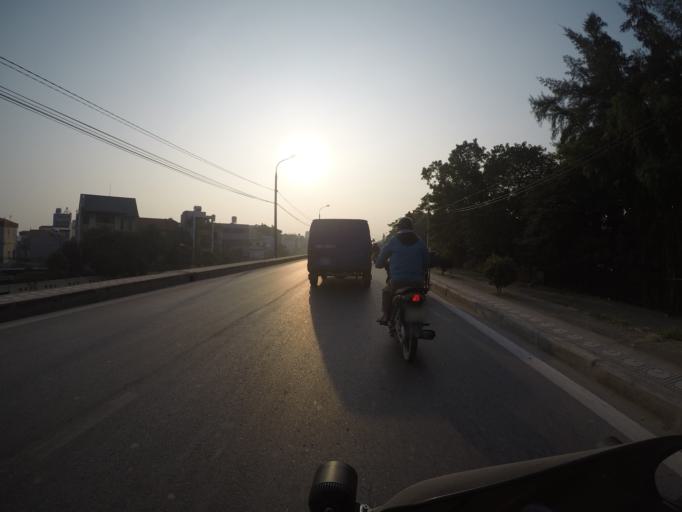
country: VN
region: Ha Noi
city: Hoan Kiem
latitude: 21.0376
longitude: 105.8691
